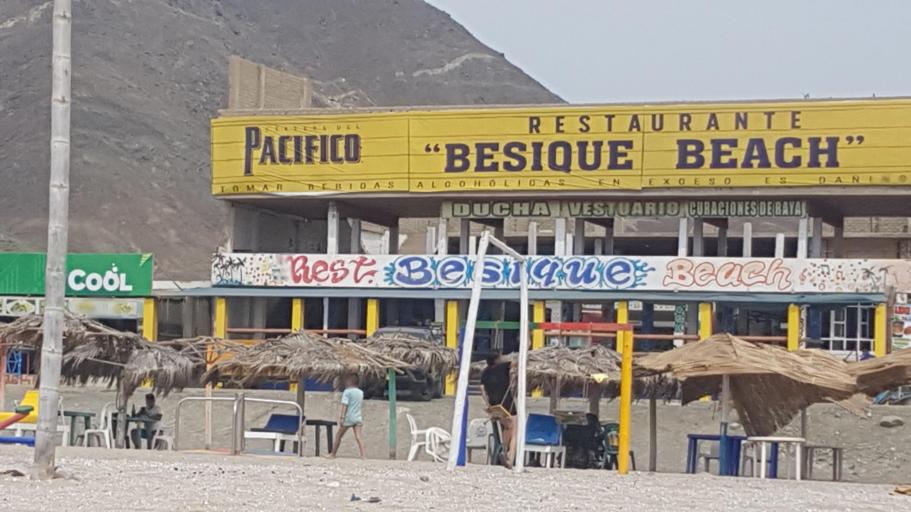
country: PE
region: Ancash
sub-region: Provincia de Santa
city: Buenos Aires
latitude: -9.1522
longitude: -78.5067
